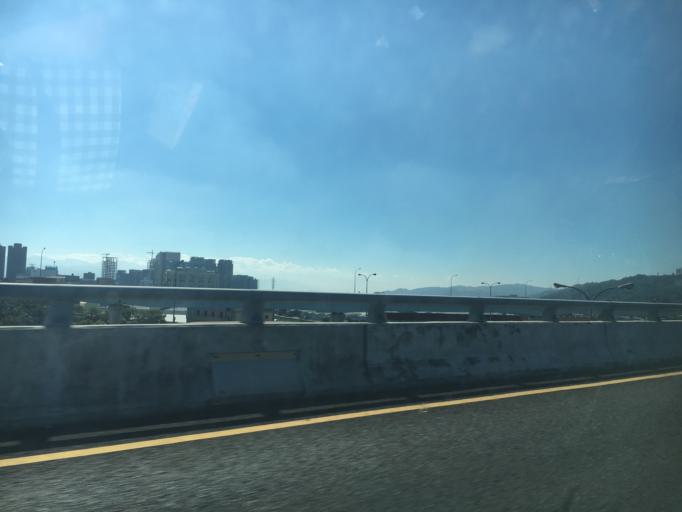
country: TW
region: Taipei
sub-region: Taipei
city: Banqiao
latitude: 25.0716
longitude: 121.4463
